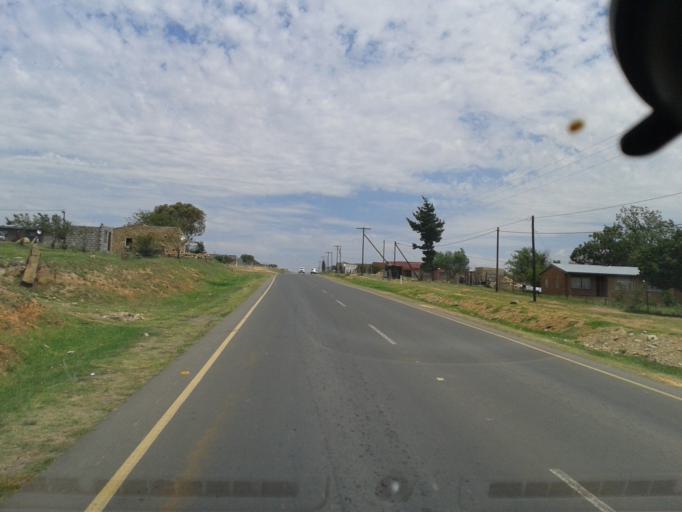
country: LS
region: Maseru
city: Maseru
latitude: -29.3557
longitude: 27.5916
